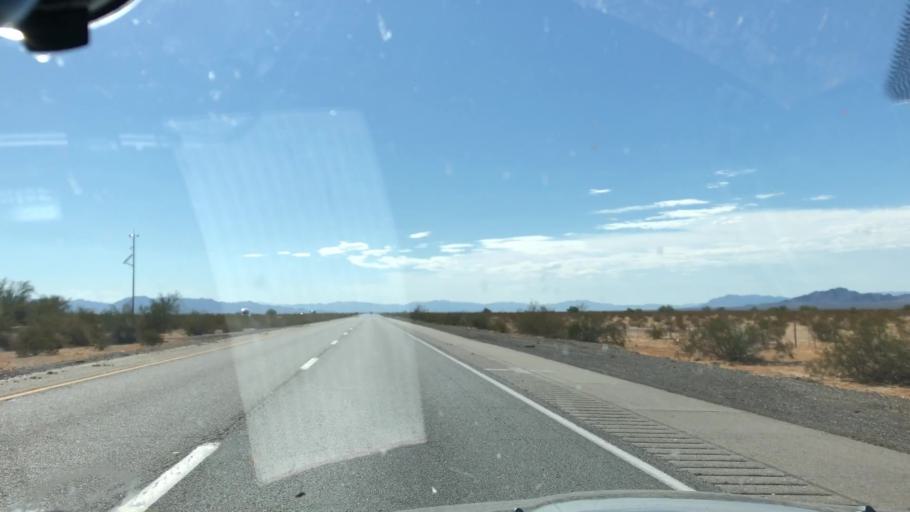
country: US
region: California
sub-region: Riverside County
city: Mesa Verde
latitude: 33.6146
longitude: -115.0135
